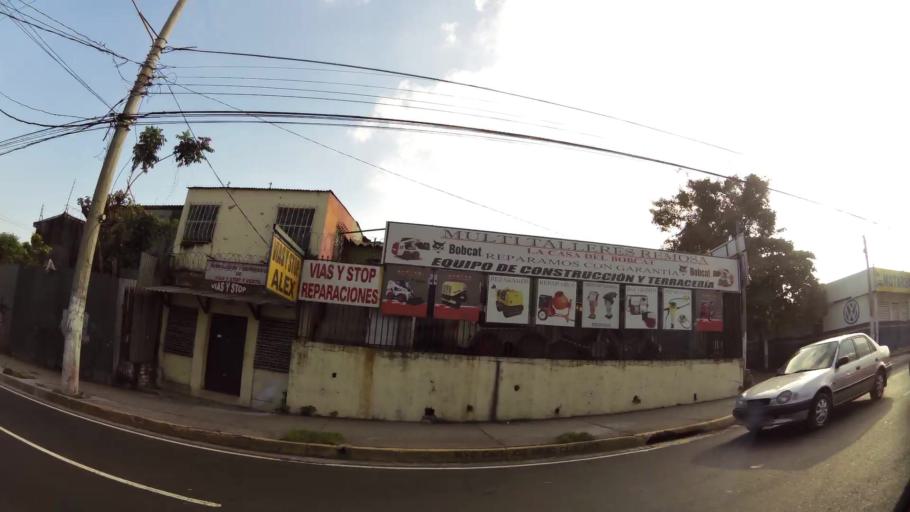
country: SV
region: San Salvador
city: San Salvador
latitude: 13.6917
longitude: -89.2136
